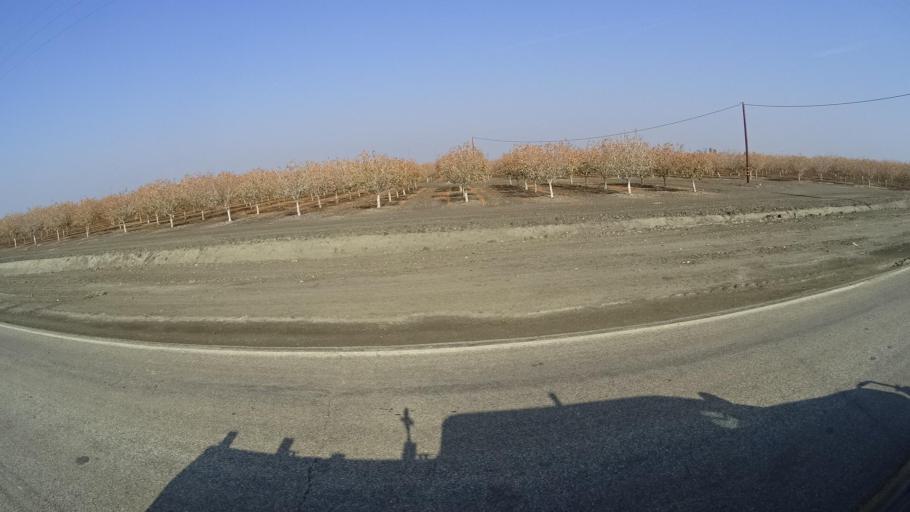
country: US
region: California
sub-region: Kern County
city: Buttonwillow
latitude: 35.3546
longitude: -119.4328
